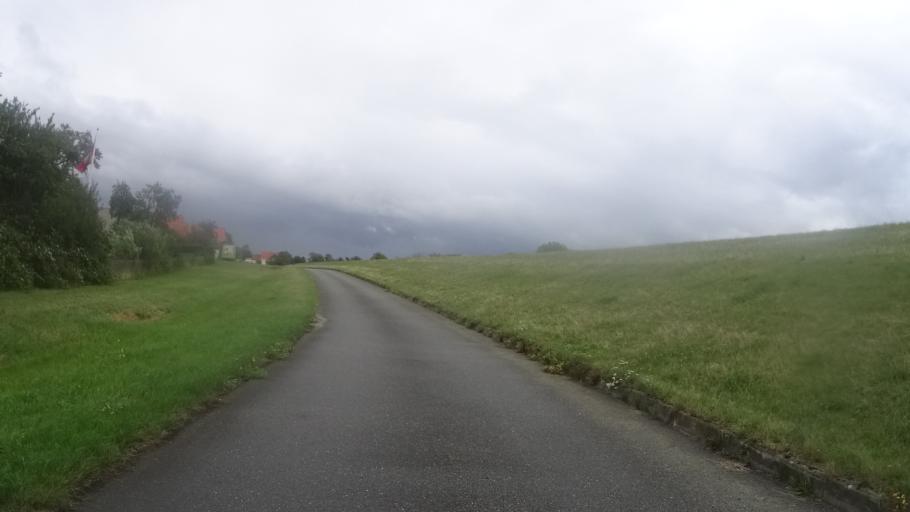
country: DE
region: Lower Saxony
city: Tosterglope
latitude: 53.2592
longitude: 10.8317
